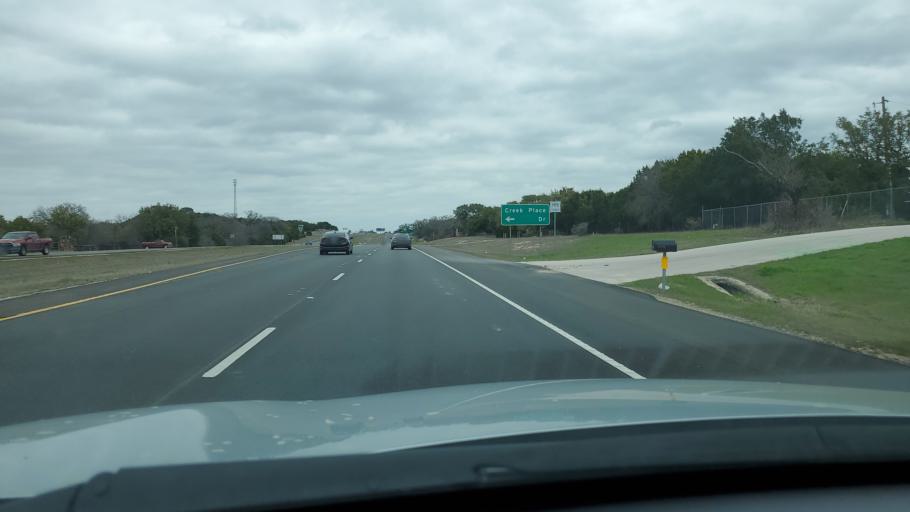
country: US
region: Texas
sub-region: Bell County
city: Killeen
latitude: 30.9982
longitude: -97.7594
